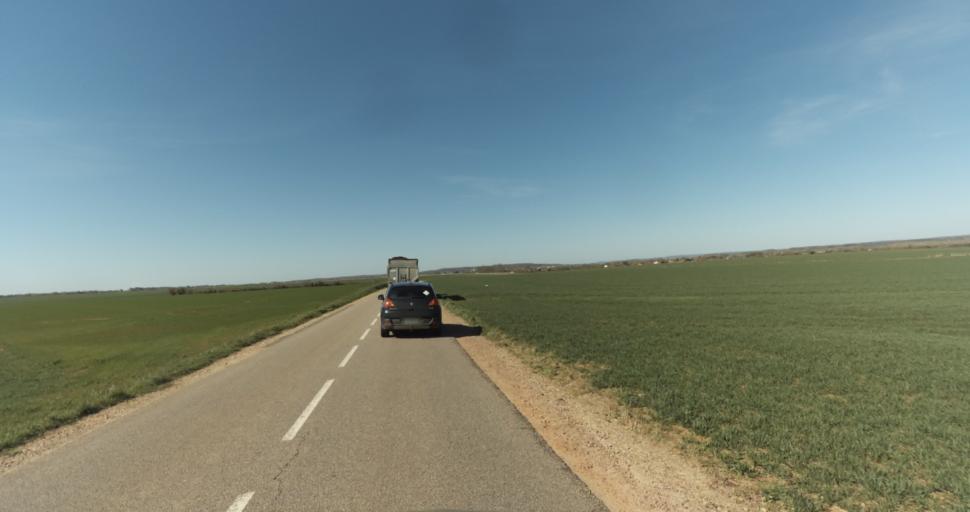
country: FR
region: Lower Normandy
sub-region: Departement du Calvados
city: Saint-Pierre-sur-Dives
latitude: 49.0398
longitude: -0.0660
